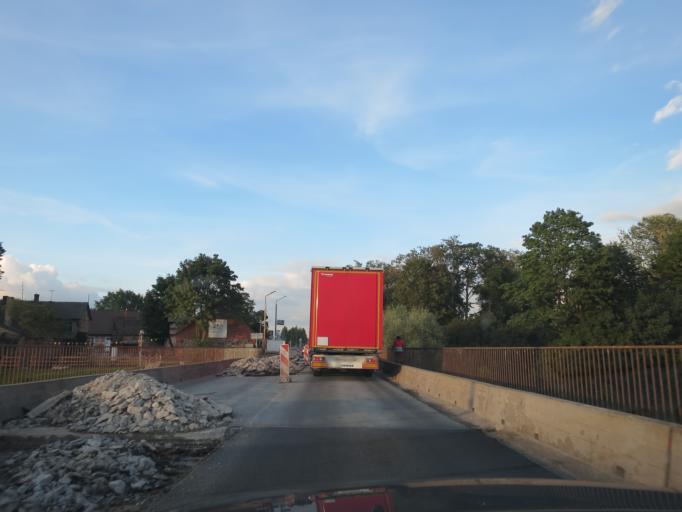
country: LV
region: Salacgrivas
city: Salacgriva
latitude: 57.7546
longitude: 24.3605
